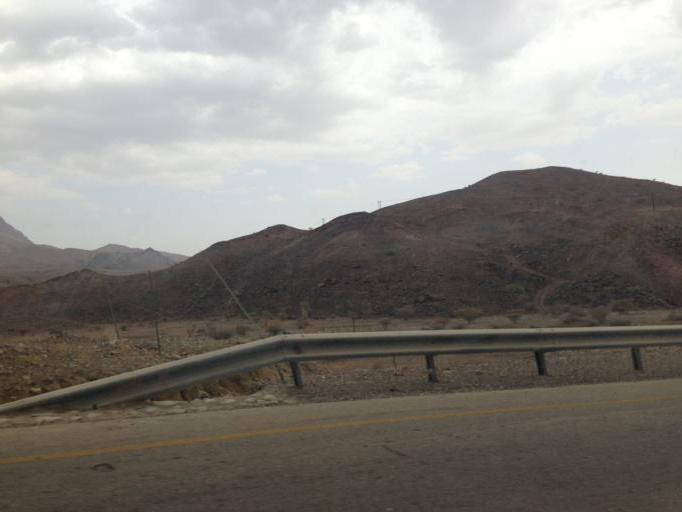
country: OM
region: Ash Sharqiyah
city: Badiyah
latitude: 22.5639
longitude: 59.0411
